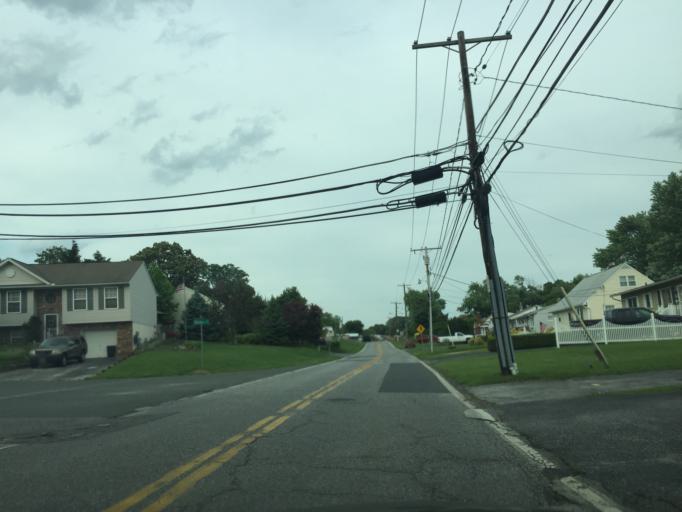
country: US
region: Maryland
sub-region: Baltimore County
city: Middle River
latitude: 39.3288
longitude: -76.4583
